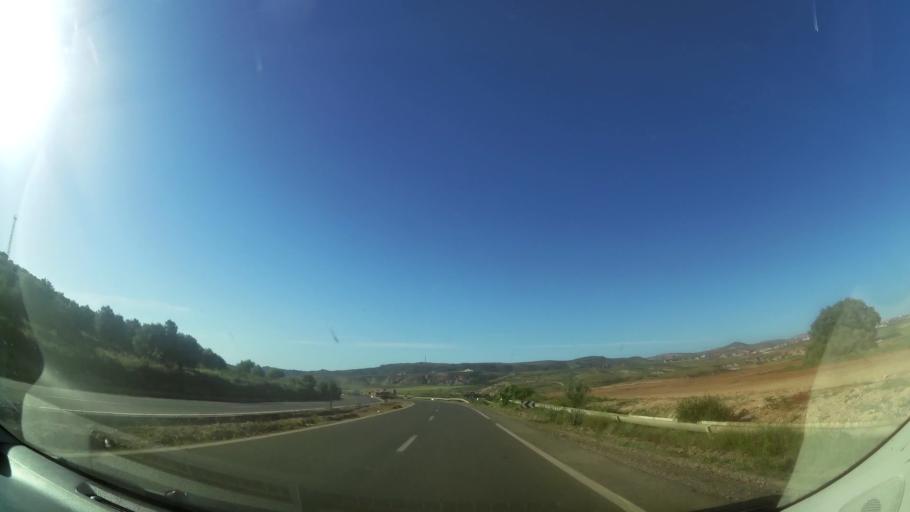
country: MA
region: Oriental
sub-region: Berkane-Taourirt
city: Ahfir
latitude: 35.0324
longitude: -2.2030
